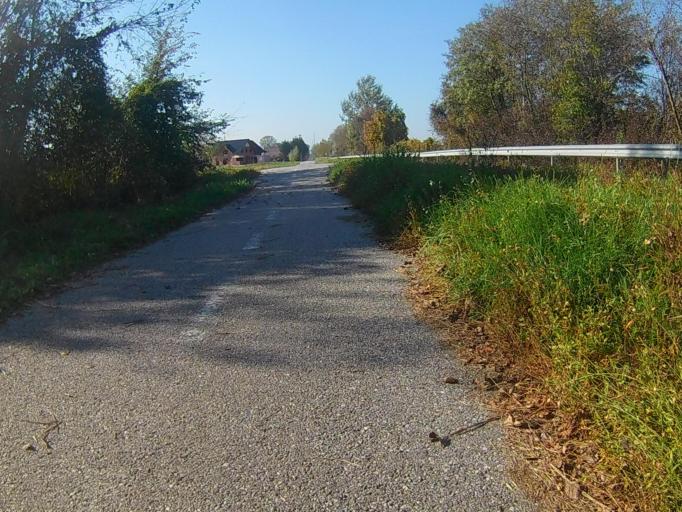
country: SI
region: Hajdina
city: Spodnja Hajdina
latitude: 46.4298
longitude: 15.8378
